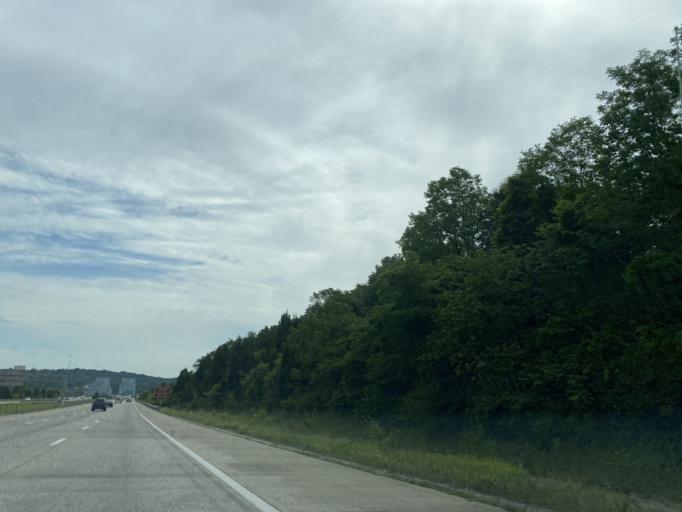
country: US
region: Kentucky
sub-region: Campbell County
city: Highland Heights
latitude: 39.0529
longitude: -84.4400
